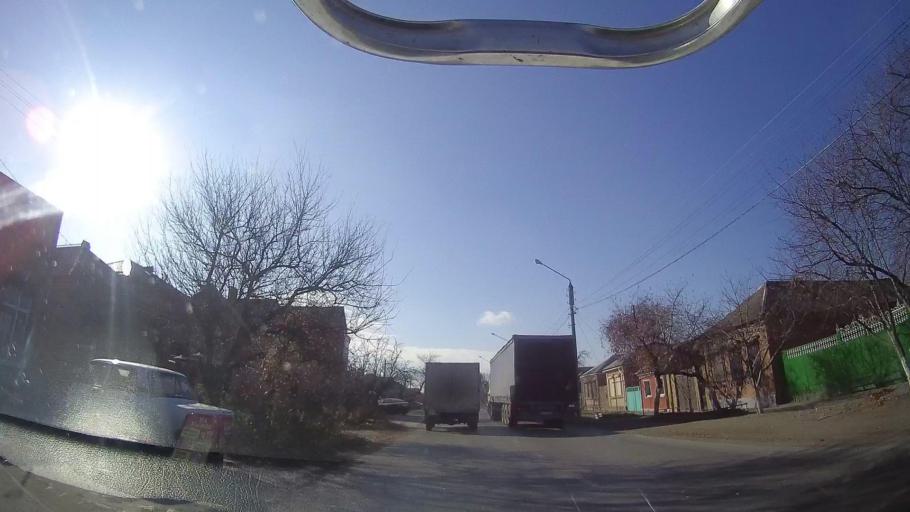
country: RU
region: Rostov
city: Bataysk
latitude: 47.1343
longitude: 39.7019
